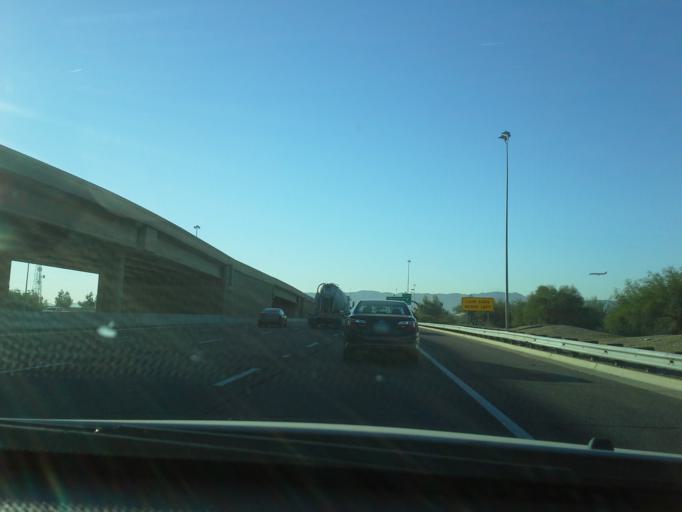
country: US
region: Arizona
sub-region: Maricopa County
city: Phoenix
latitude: 33.4529
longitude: -112.0377
